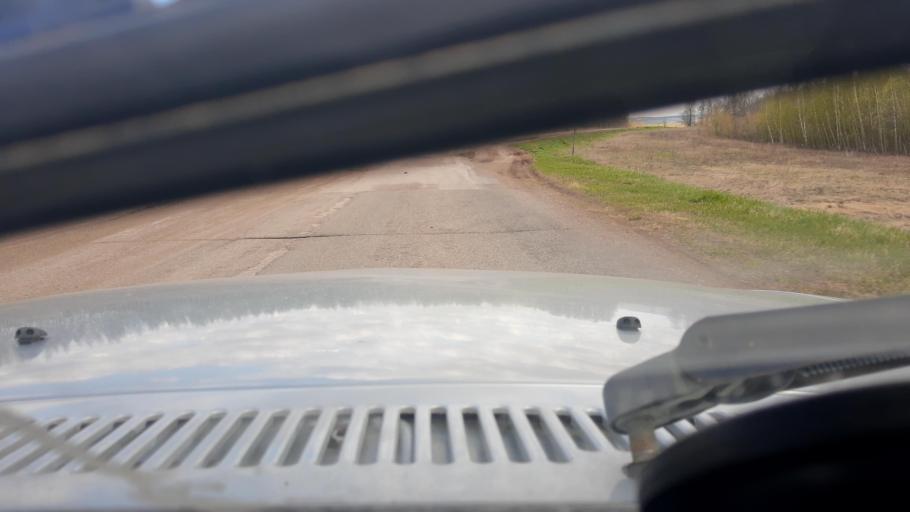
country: RU
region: Bashkortostan
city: Yazykovo
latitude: 55.2717
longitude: 56.2546
